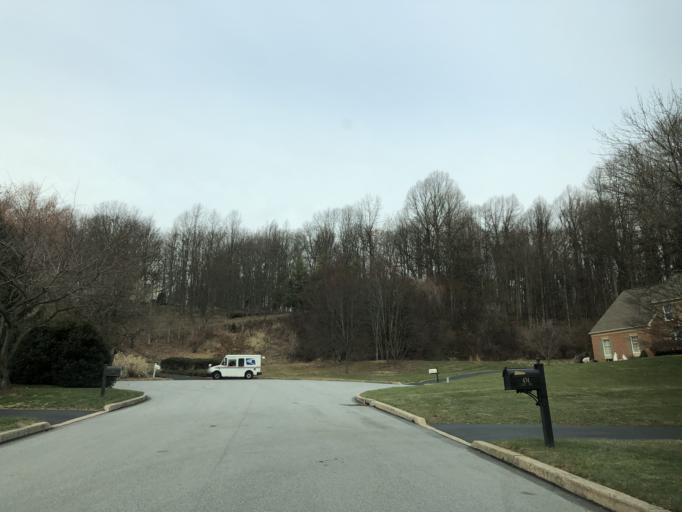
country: US
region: Pennsylvania
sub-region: Chester County
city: Exton
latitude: 40.0383
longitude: -75.6415
